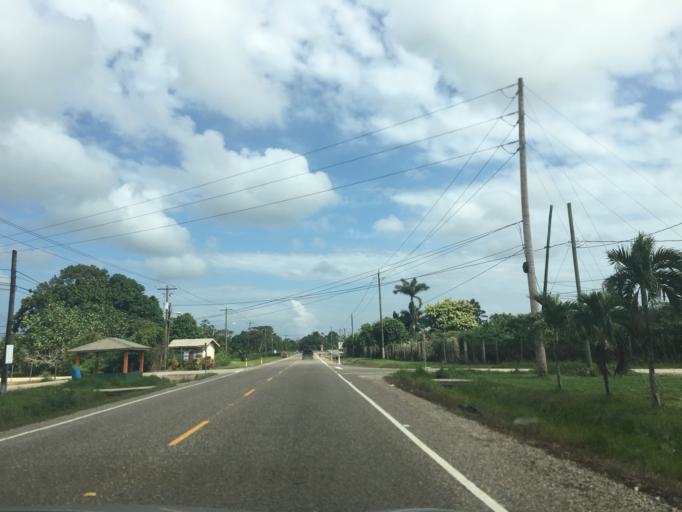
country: BZ
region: Stann Creek
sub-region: Dangriga
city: Dangriga
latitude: 17.0010
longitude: -88.3107
